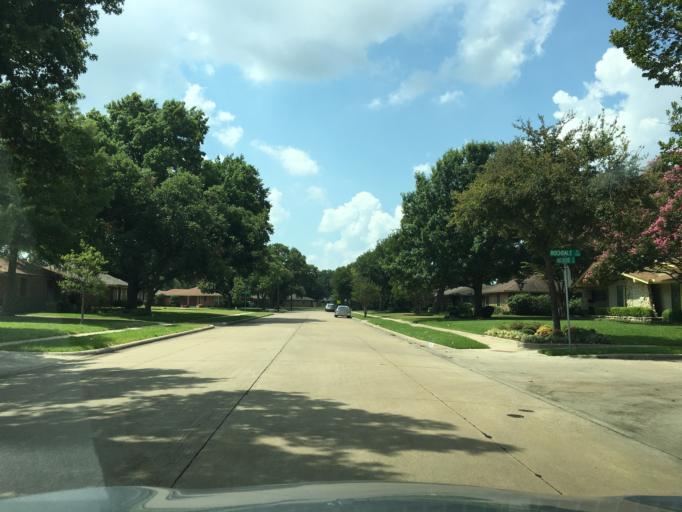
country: US
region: Texas
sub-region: Dallas County
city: Garland
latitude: 32.9365
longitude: -96.6424
